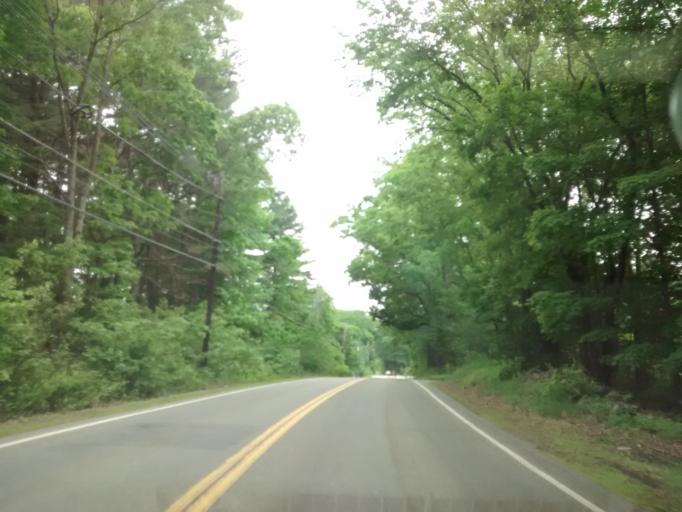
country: US
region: Massachusetts
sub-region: Worcester County
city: Grafton
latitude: 42.2429
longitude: -71.6960
